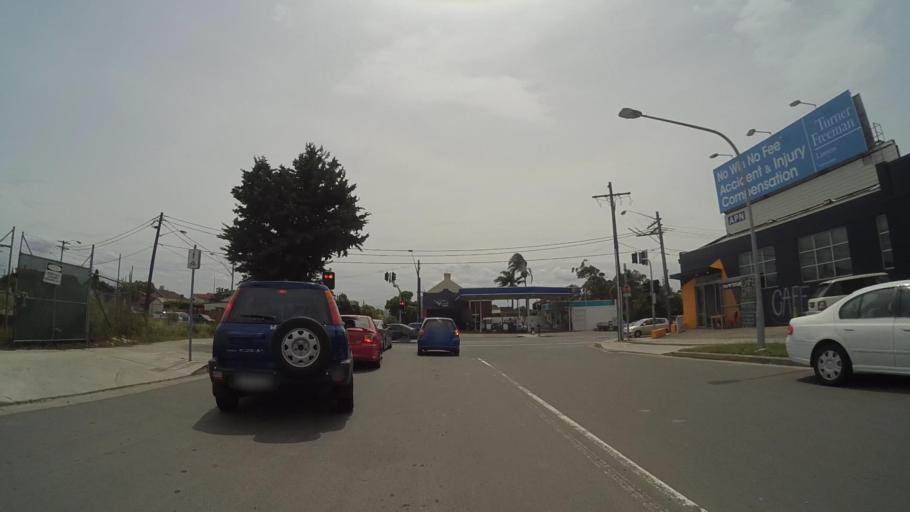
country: AU
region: New South Wales
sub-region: Marrickville
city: Marrickville
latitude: -33.9208
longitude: 151.1679
